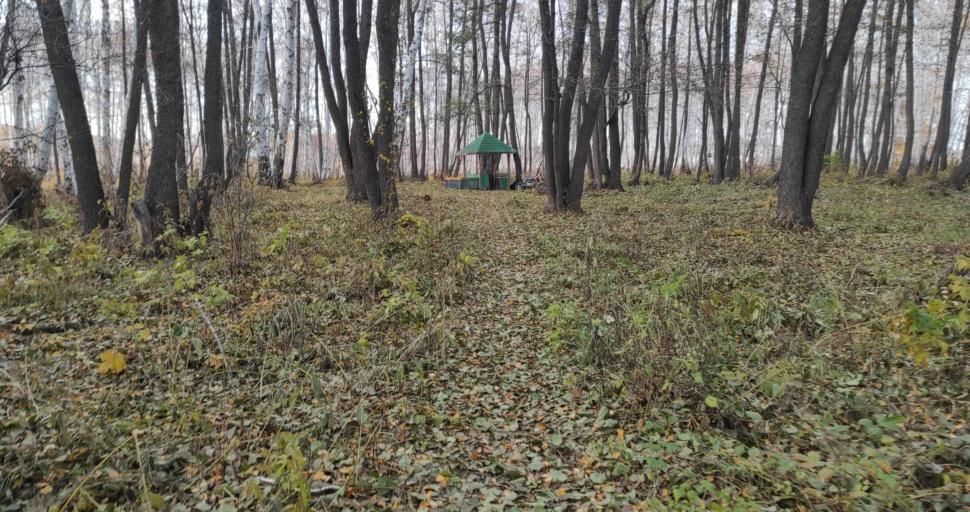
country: RU
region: Bashkortostan
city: Sibay
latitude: 52.6544
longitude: 58.5704
